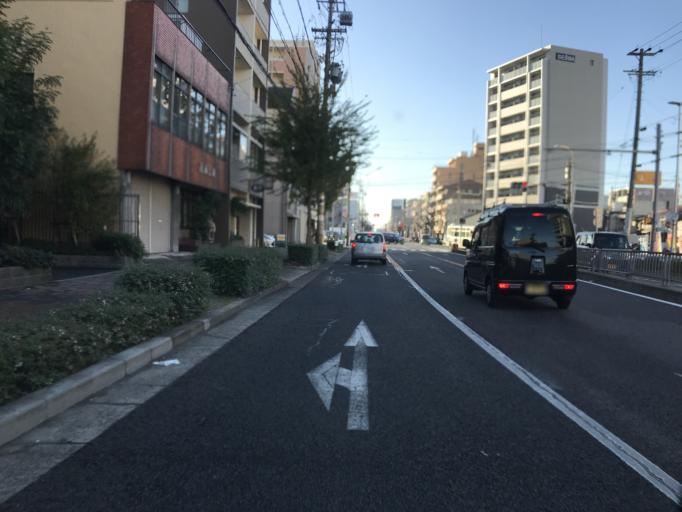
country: JP
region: Aichi
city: Nagoya-shi
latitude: 35.1775
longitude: 136.8687
